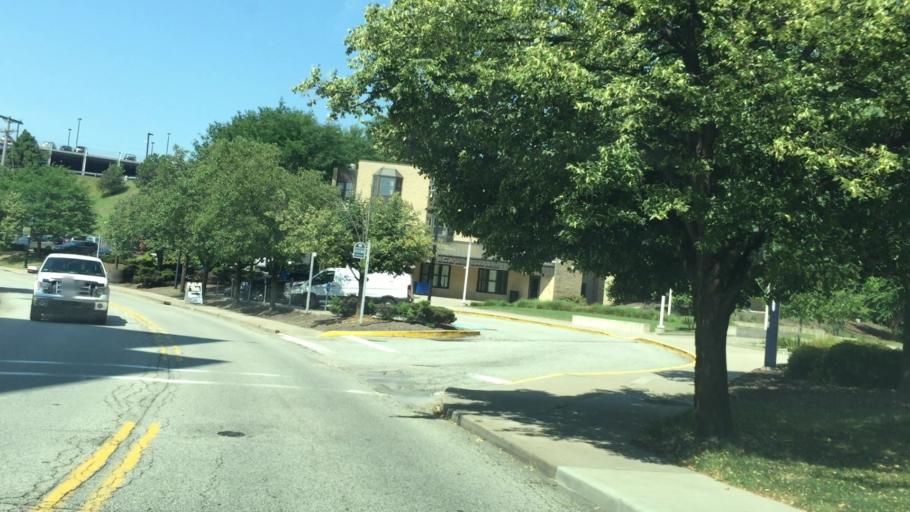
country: US
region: Pennsylvania
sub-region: Allegheny County
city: Bloomfield
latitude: 40.4455
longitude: -79.9622
